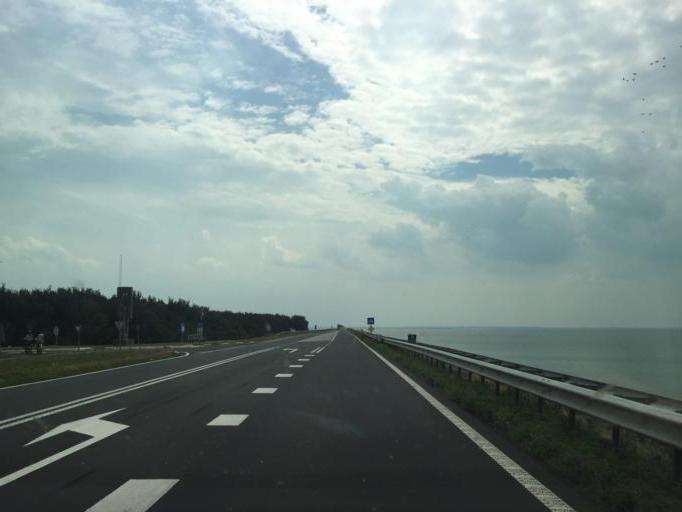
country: NL
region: North Holland
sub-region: Gemeente Enkhuizen
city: Enkhuizen
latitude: 52.6362
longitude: 5.4125
